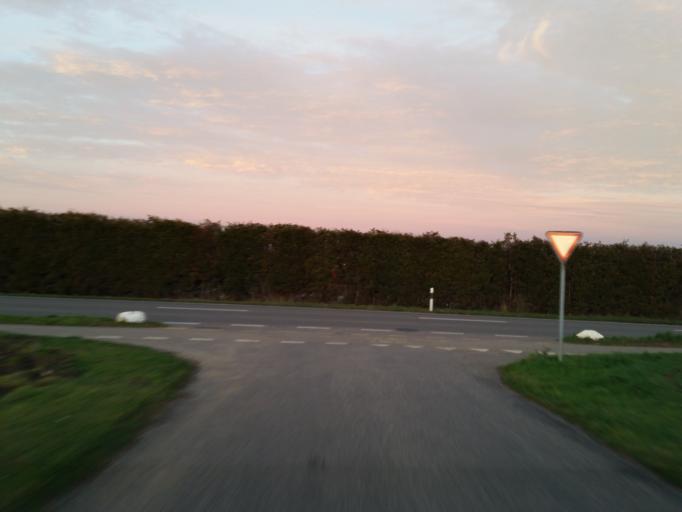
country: CH
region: Thurgau
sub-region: Arbon District
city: Uttwil
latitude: 47.5909
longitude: 9.3241
